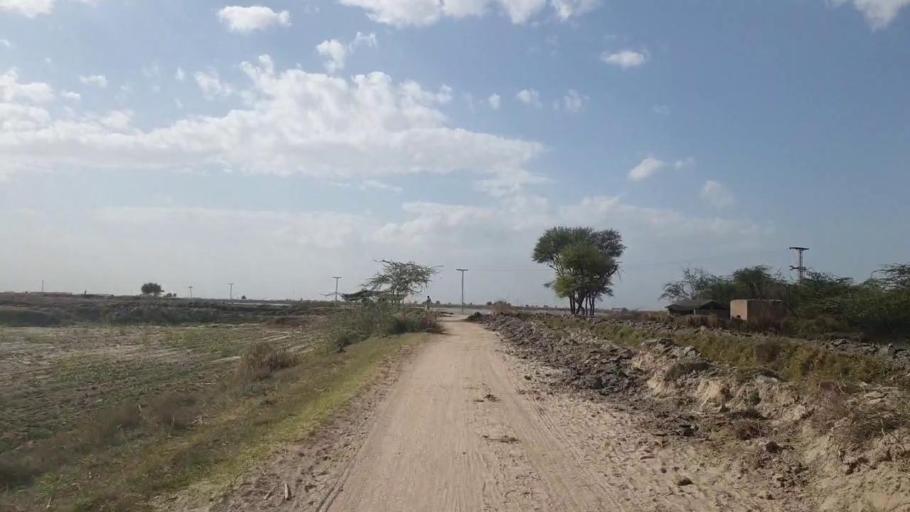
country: PK
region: Sindh
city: Shahdadpur
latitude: 25.9893
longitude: 68.4674
